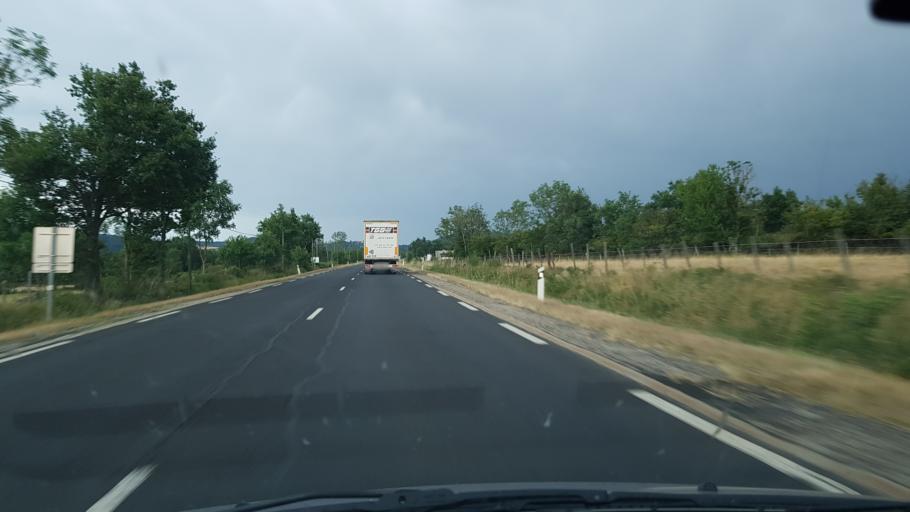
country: FR
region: Auvergne
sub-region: Departement de la Haute-Loire
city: Langeac
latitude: 45.1421
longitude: 3.5684
